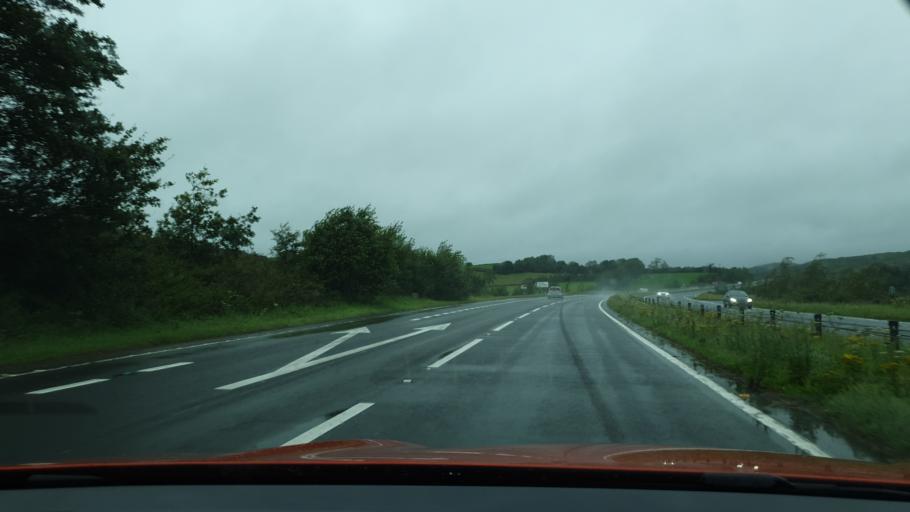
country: GB
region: England
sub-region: Cumbria
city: Grange-over-Sands
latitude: 54.2268
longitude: -2.9105
